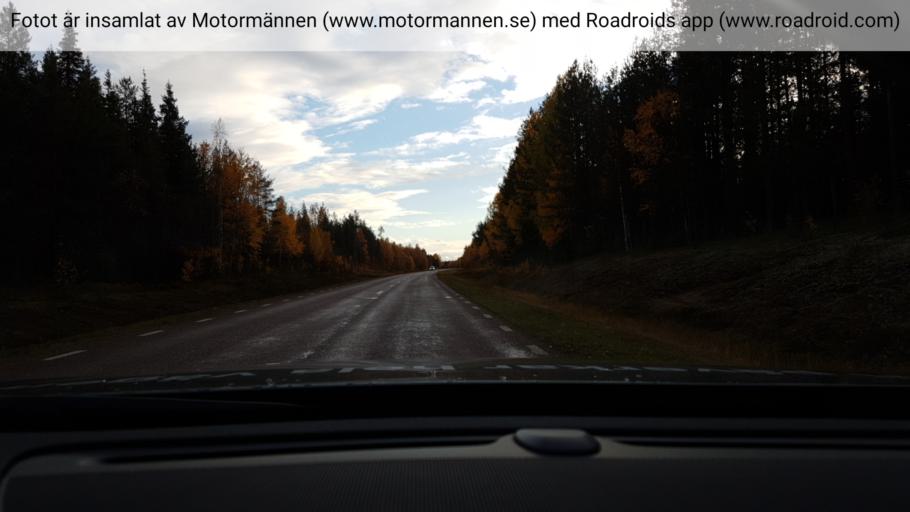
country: SE
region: Norrbotten
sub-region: Pajala Kommun
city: Pajala
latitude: 67.1474
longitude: 22.6237
